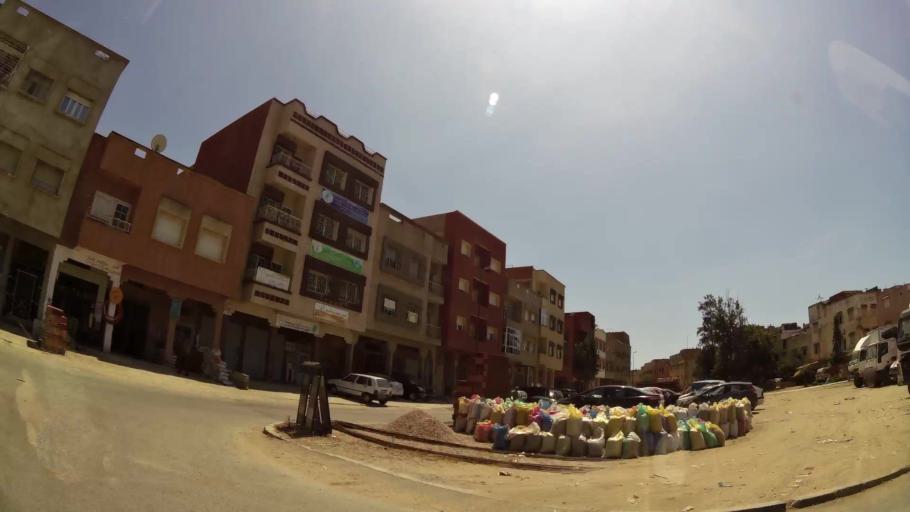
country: MA
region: Gharb-Chrarda-Beni Hssen
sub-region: Kenitra Province
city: Kenitra
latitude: 34.2499
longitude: -6.5385
